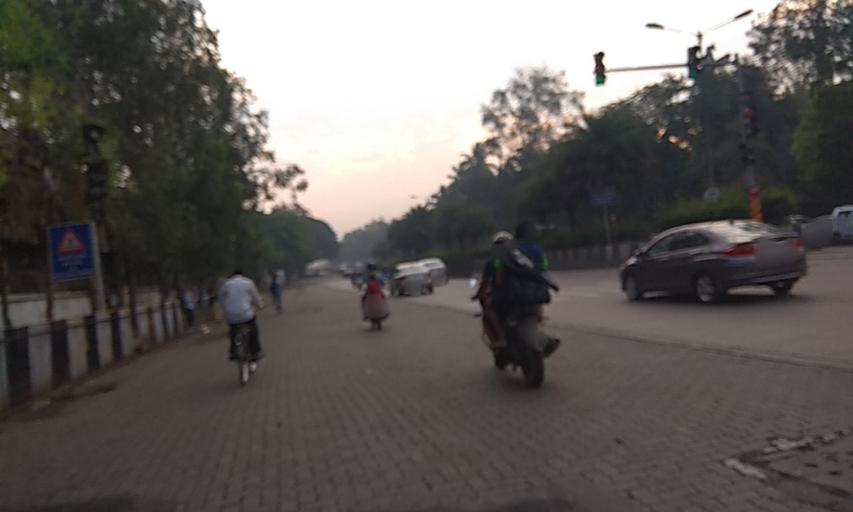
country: IN
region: Maharashtra
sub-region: Pune Division
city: Khadki
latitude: 18.5527
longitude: 73.8974
